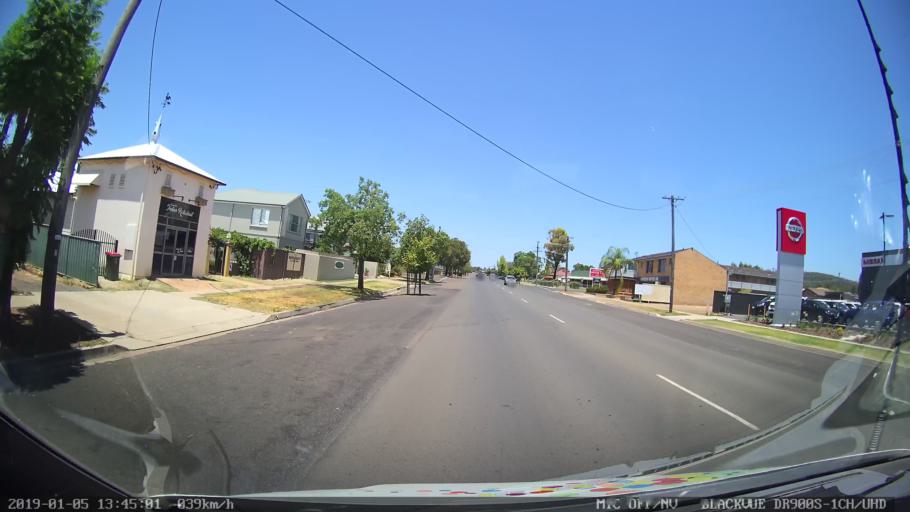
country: AU
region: New South Wales
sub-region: Gunnedah
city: Gunnedah
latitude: -30.9815
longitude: 150.2595
